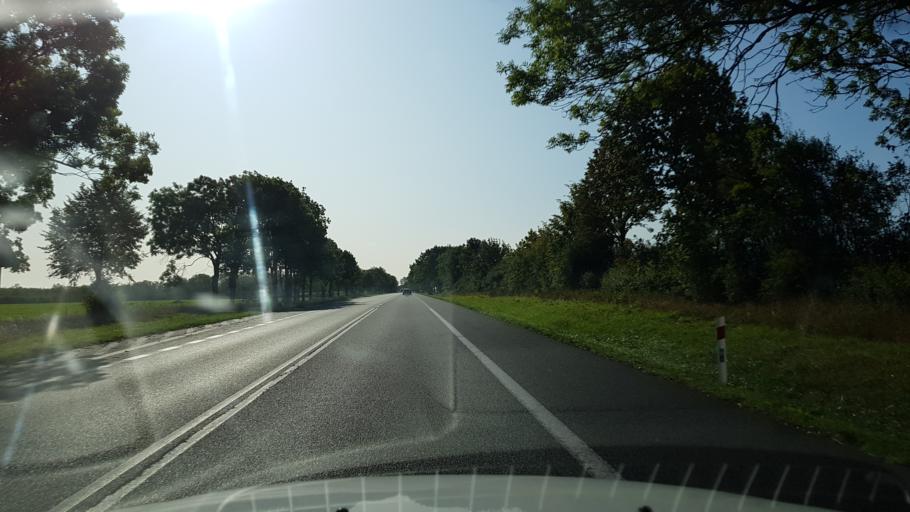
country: PL
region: West Pomeranian Voivodeship
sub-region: Powiat pyrzycki
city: Pyrzyce
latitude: 53.1739
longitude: 14.8515
